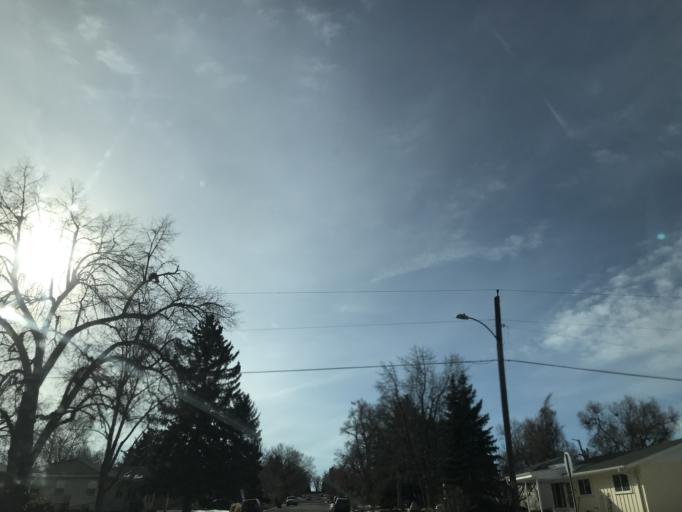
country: US
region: Colorado
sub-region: Arapahoe County
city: Littleton
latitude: 39.6007
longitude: -105.0093
